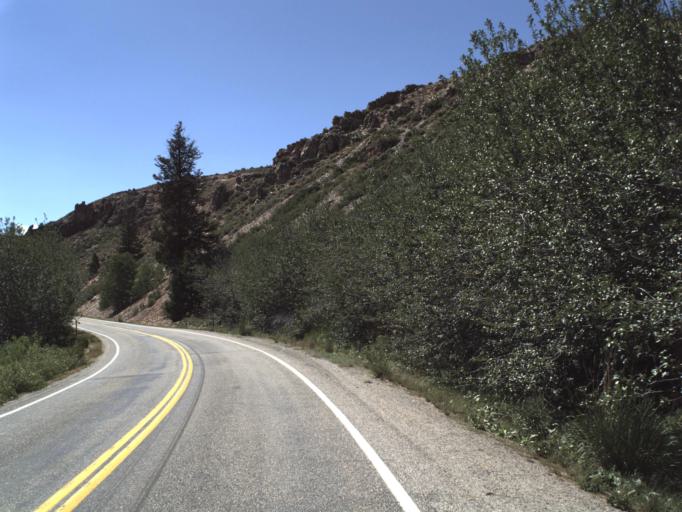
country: US
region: Utah
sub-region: Rich County
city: Randolph
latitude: 41.4820
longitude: -111.3750
